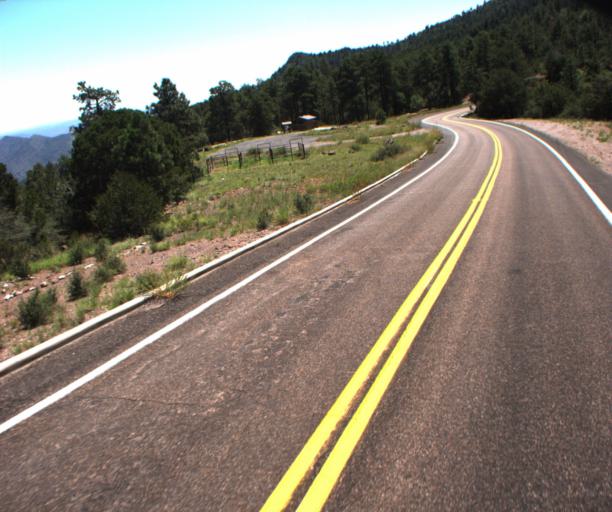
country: US
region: Arizona
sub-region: Greenlee County
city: Morenci
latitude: 33.2111
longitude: -109.3762
